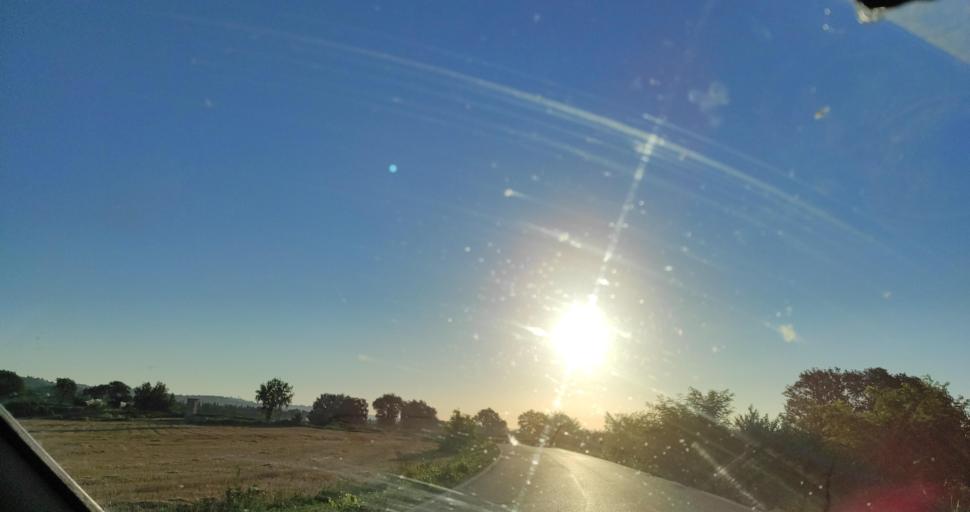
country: IT
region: The Marches
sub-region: Provincia di Macerata
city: Casette Verdini
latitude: 43.2327
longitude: 13.3767
